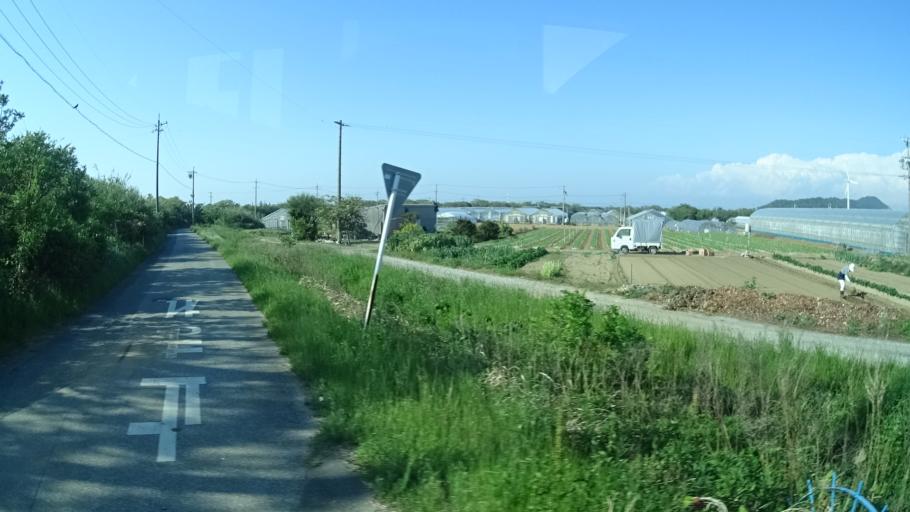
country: JP
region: Aichi
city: Toyohama
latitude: 34.5897
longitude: 137.0401
